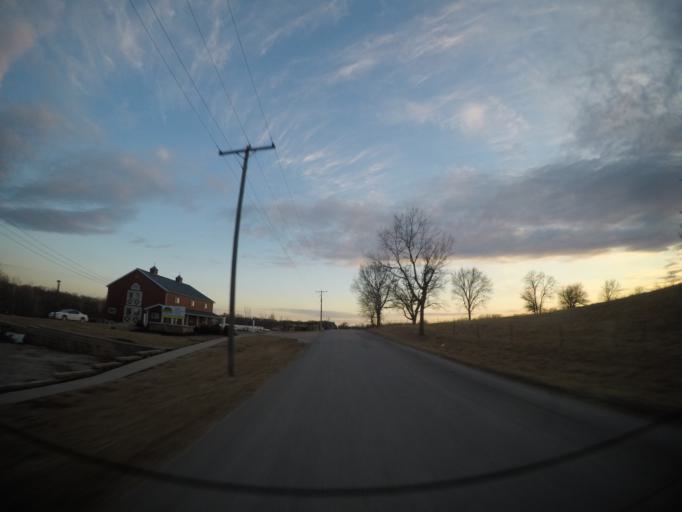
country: US
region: Kansas
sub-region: Wyandotte County
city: Bonner Springs
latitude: 39.0550
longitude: -94.9088
